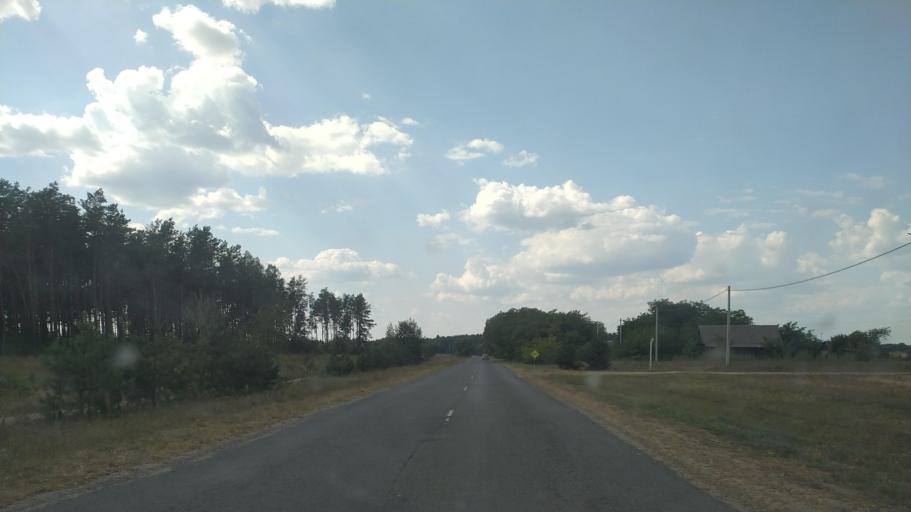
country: BY
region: Brest
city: Drahichyn
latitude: 52.1030
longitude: 25.1347
